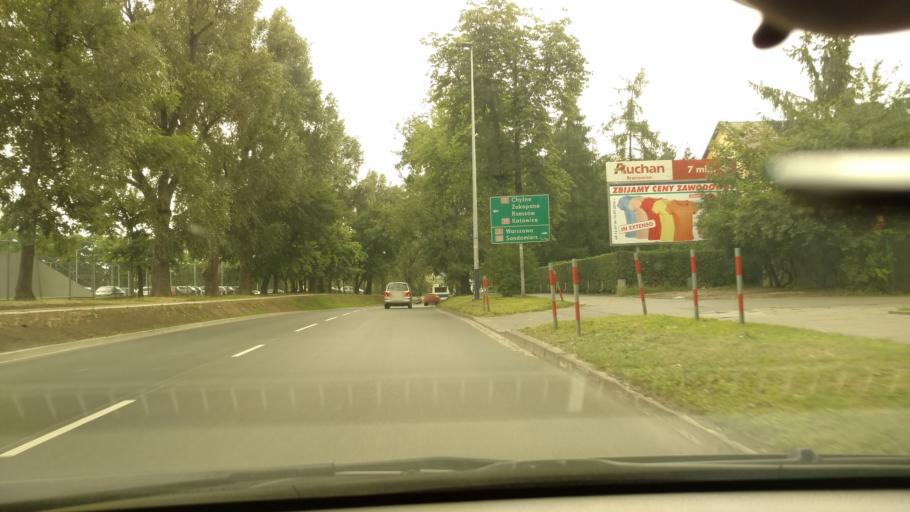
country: PL
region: Lesser Poland Voivodeship
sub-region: Krakow
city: Krakow
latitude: 50.0897
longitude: 19.9389
